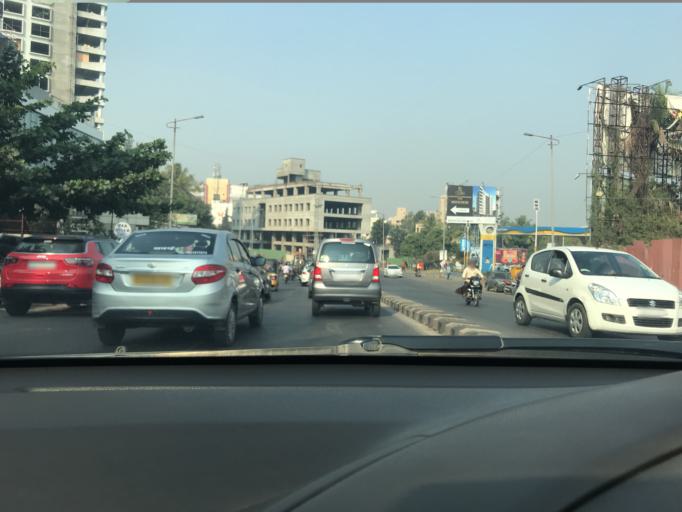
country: IN
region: Maharashtra
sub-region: Pune Division
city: Khadki
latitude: 18.5549
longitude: 73.8005
